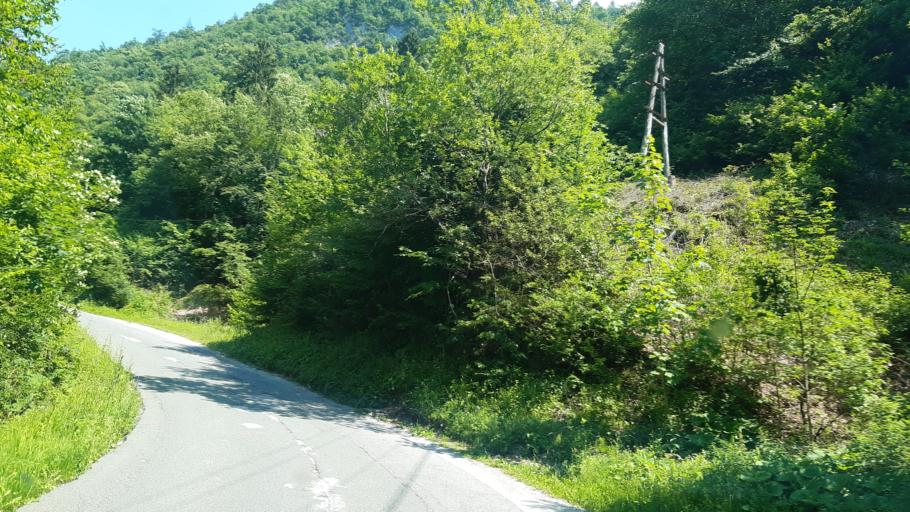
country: SI
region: Cerklje na Gorenjskem
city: Cerklje na Gorenjskem
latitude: 46.2784
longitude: 14.4972
